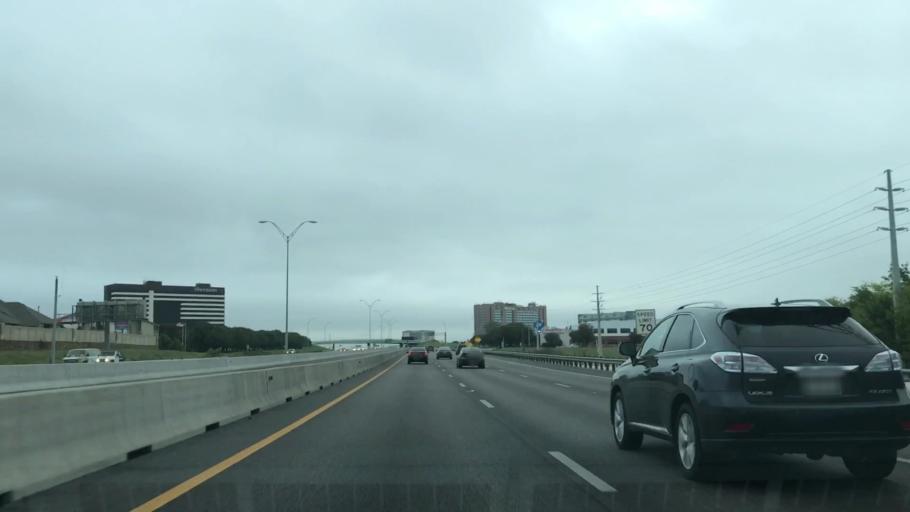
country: US
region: Texas
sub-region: Dallas County
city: Coppell
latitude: 32.9117
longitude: -97.0018
